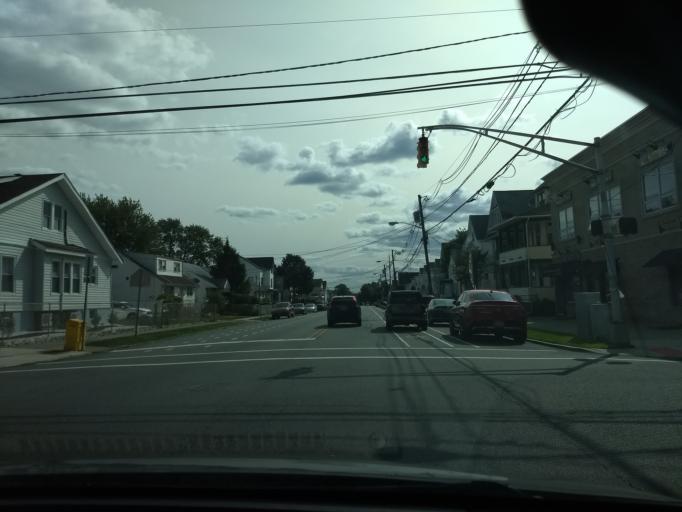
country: US
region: New Jersey
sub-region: Passaic County
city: Hawthorne
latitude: 40.9322
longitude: -74.1495
